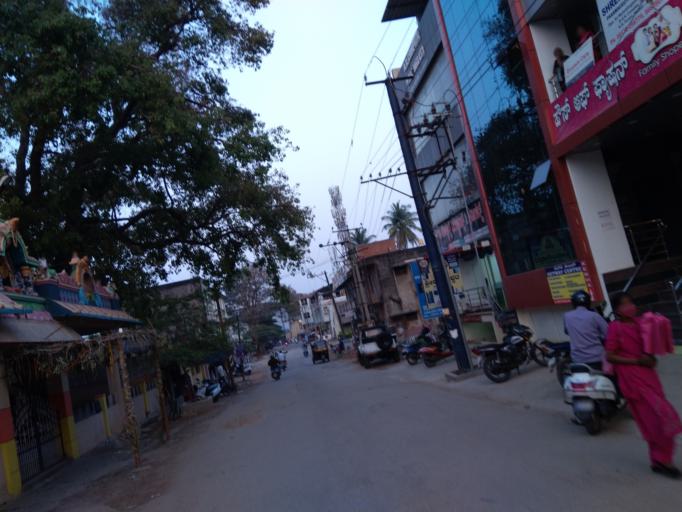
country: IN
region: Karnataka
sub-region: Hassan
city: Hassan
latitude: 13.0085
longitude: 76.1084
